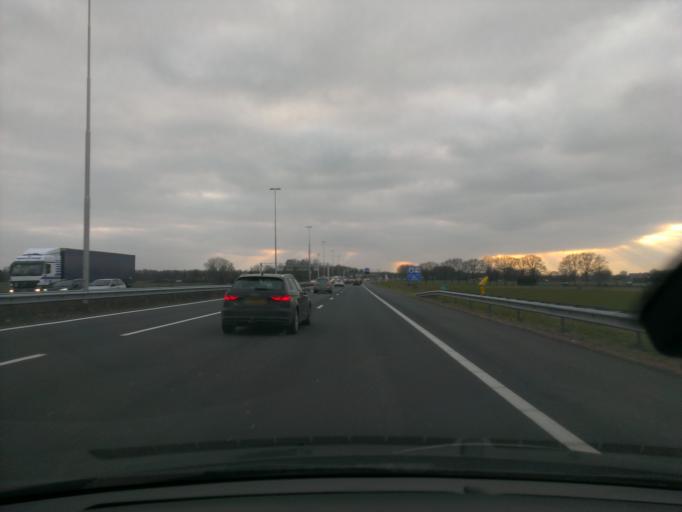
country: NL
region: Gelderland
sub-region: Gemeente Voorst
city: Twello
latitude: 52.2133
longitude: 6.1061
